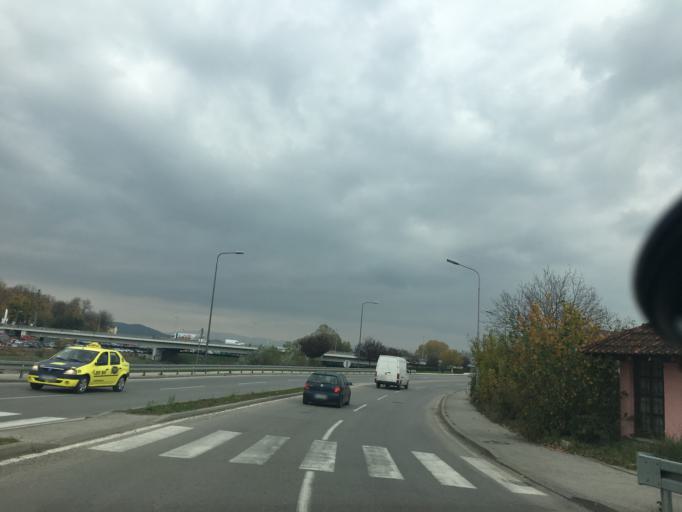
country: RS
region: Central Serbia
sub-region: Raski Okrug
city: Kraljevo
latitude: 43.7186
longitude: 20.6867
